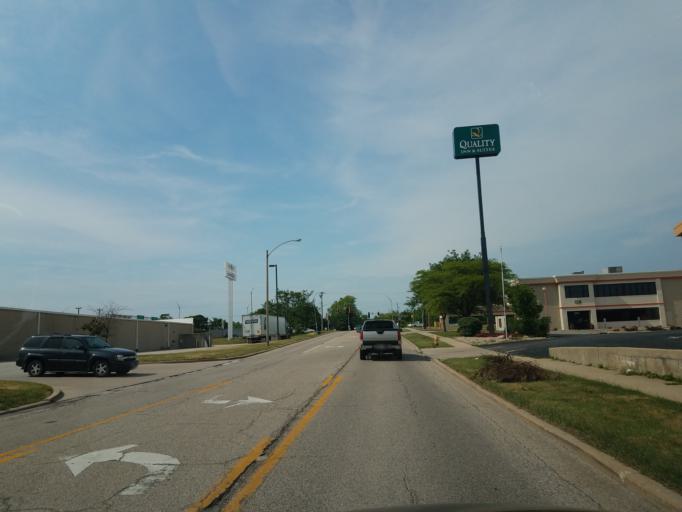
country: US
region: Illinois
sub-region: McLean County
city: Bloomington
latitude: 40.4867
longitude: -88.9494
